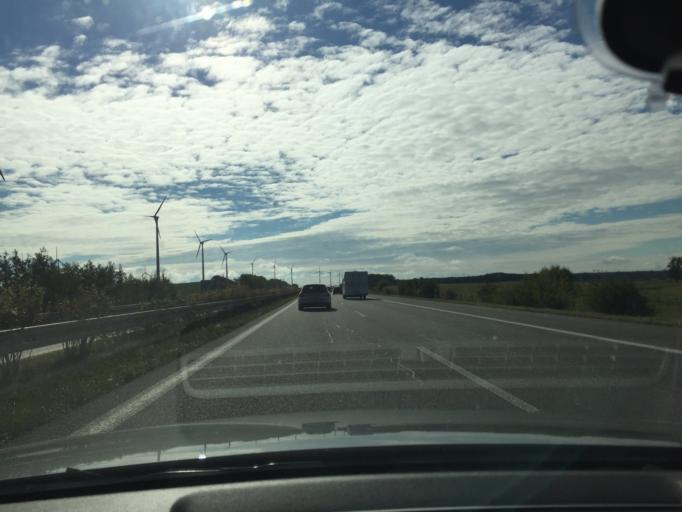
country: DE
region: Mecklenburg-Vorpommern
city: Robel
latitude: 53.3404
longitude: 12.4748
